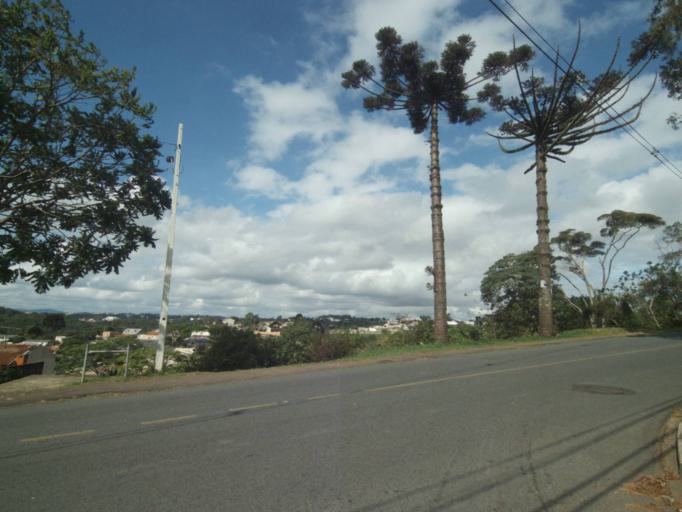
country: BR
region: Parana
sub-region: Curitiba
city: Curitiba
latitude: -25.3823
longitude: -49.2943
